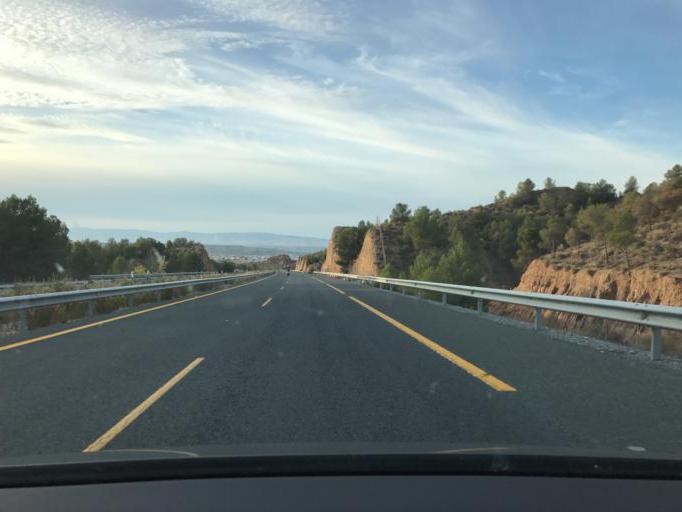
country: ES
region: Andalusia
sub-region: Provincia de Granada
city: Guadix
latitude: 37.2852
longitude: -3.1028
